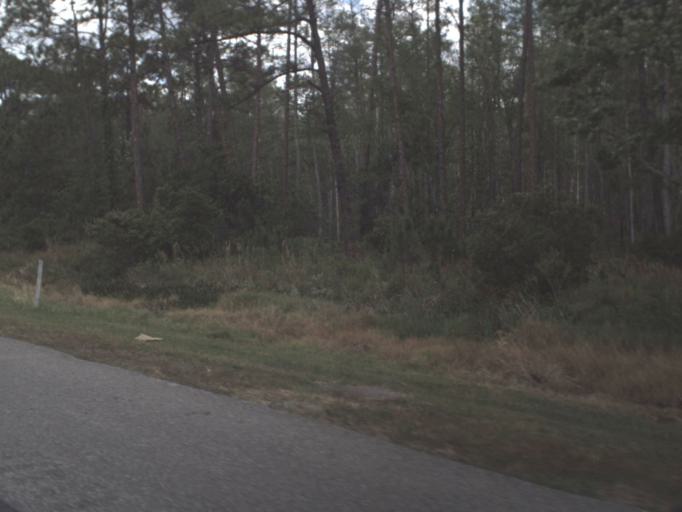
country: US
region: Florida
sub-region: Orange County
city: Wedgefield
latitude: 28.4518
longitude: -81.1848
